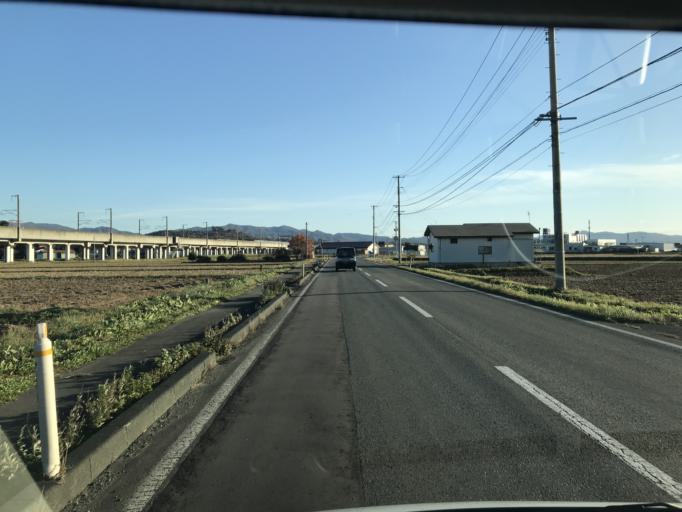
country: JP
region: Iwate
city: Mizusawa
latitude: 39.1671
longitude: 141.1796
